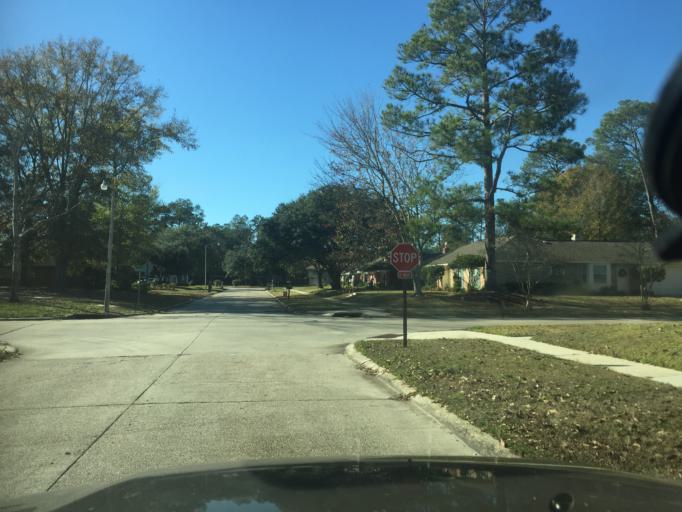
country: US
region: Louisiana
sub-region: Saint Tammany Parish
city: Slidell
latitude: 30.2999
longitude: -89.7494
